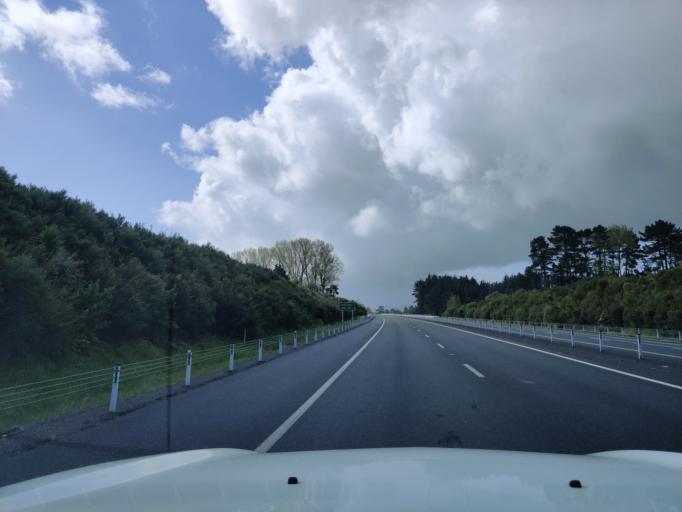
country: NZ
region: Waikato
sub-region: Waipa District
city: Cambridge
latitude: -37.8861
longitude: 175.4940
